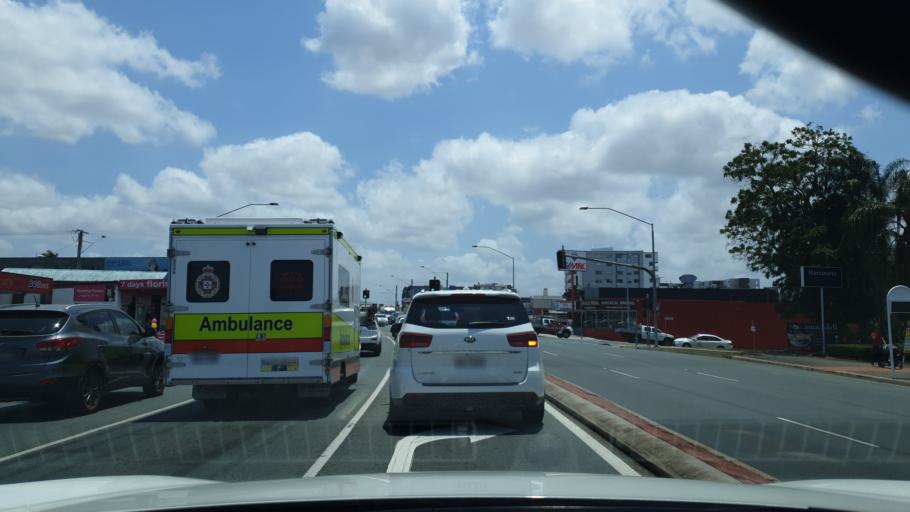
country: AU
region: Queensland
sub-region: Brisbane
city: Wavell Heights
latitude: -27.3905
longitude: 153.0314
